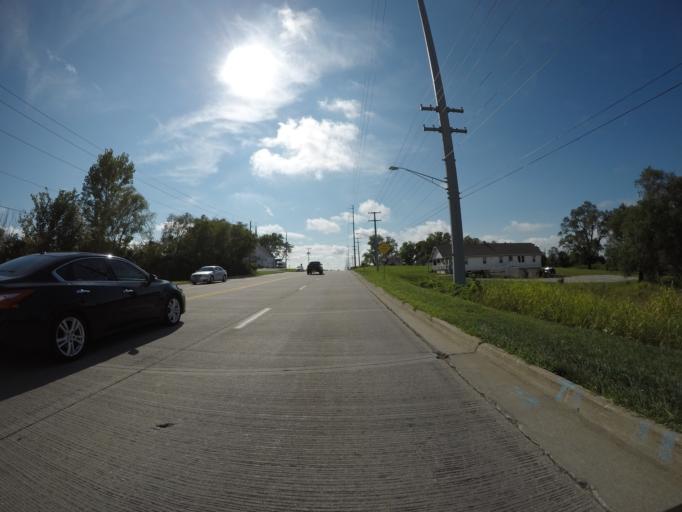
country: US
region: Kansas
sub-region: Wyandotte County
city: Edwardsville
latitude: 39.1287
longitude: -94.8387
